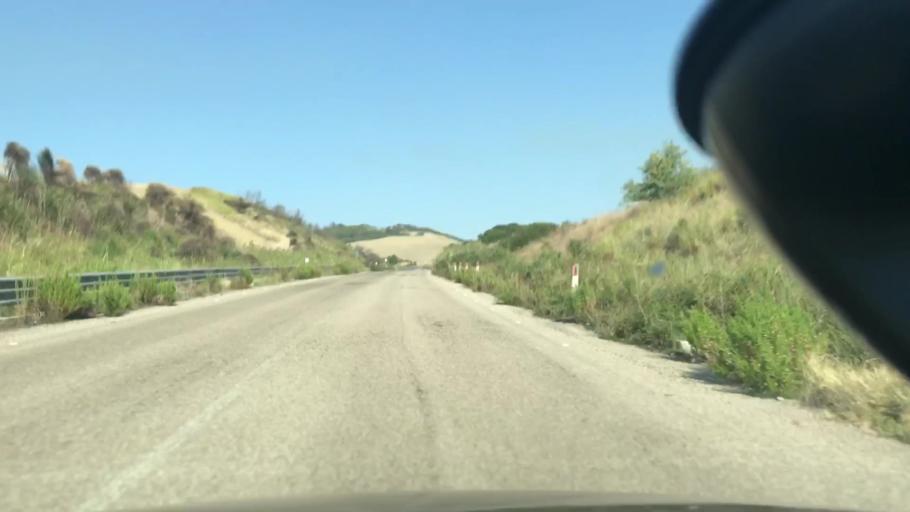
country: IT
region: Basilicate
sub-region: Provincia di Matera
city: Grottole
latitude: 40.6957
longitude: 16.4247
